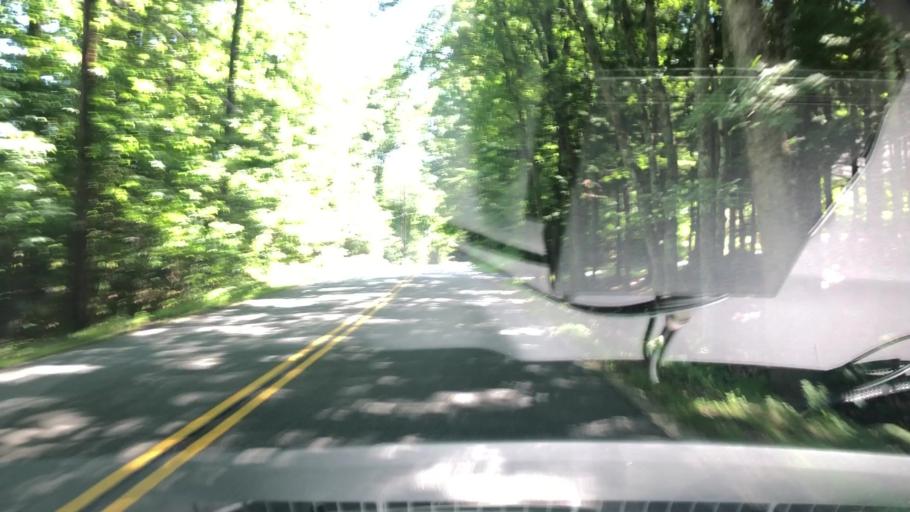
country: US
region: New Hampshire
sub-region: Hillsborough County
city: Milford
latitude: 42.8649
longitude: -71.6041
